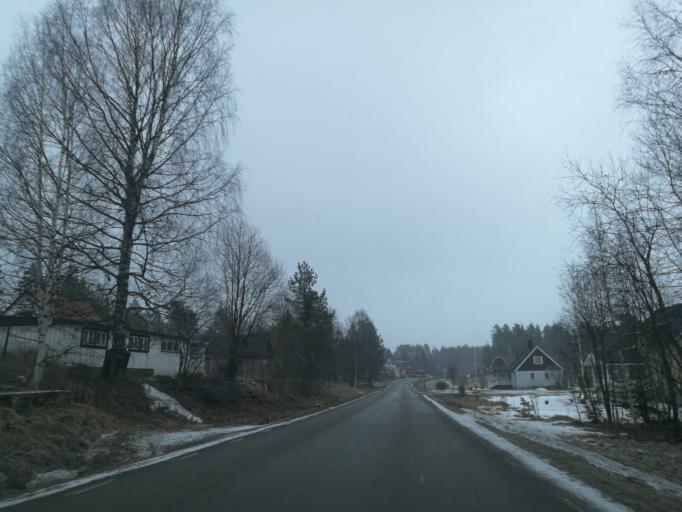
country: NO
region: Hedmark
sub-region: Grue
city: Kirkenaer
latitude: 60.7022
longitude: 12.5907
